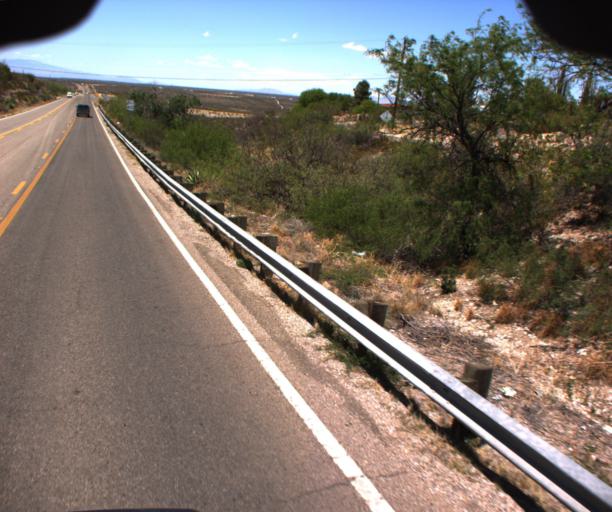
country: US
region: Arizona
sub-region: Cochise County
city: Tombstone
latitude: 31.7204
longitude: -110.0713
